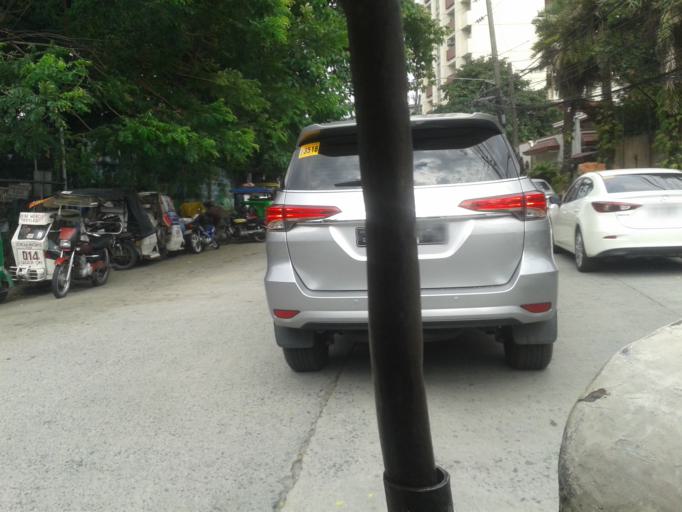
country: PH
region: Metro Manila
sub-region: Quezon City
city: Quezon City
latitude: 14.6417
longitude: 121.0735
